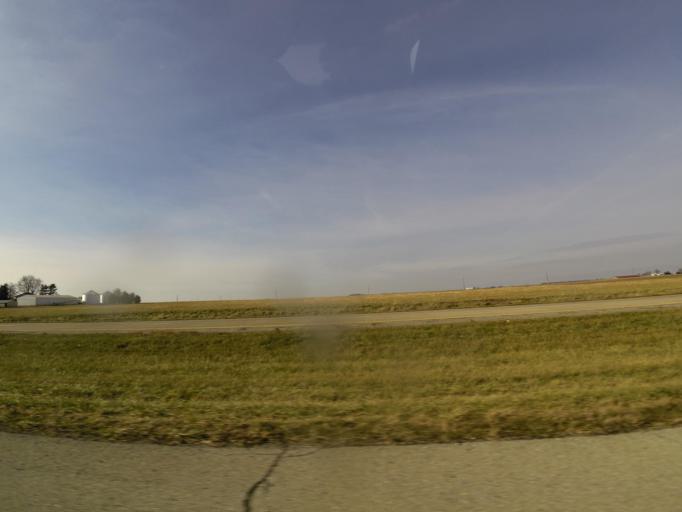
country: US
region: Illinois
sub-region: Macon County
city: Maroa
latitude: 40.0696
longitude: -88.9656
